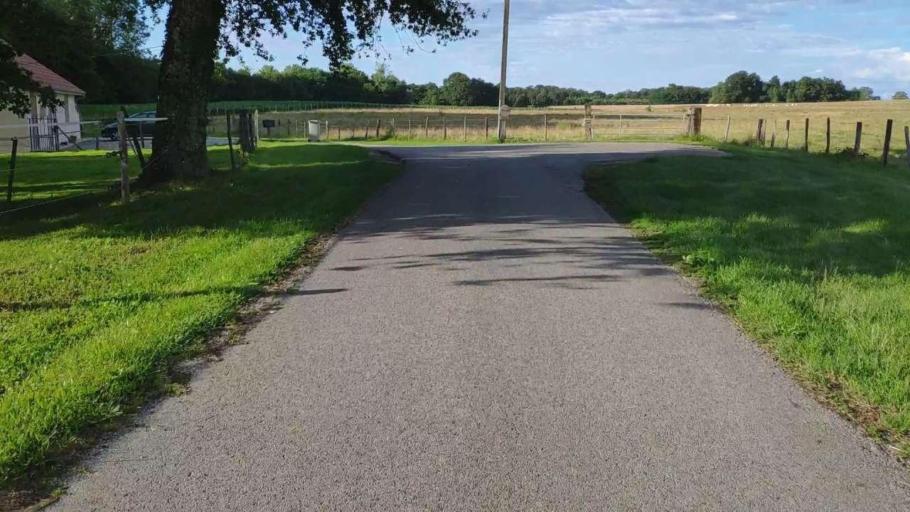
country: FR
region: Franche-Comte
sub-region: Departement du Jura
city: Bletterans
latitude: 46.7847
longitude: 5.4953
